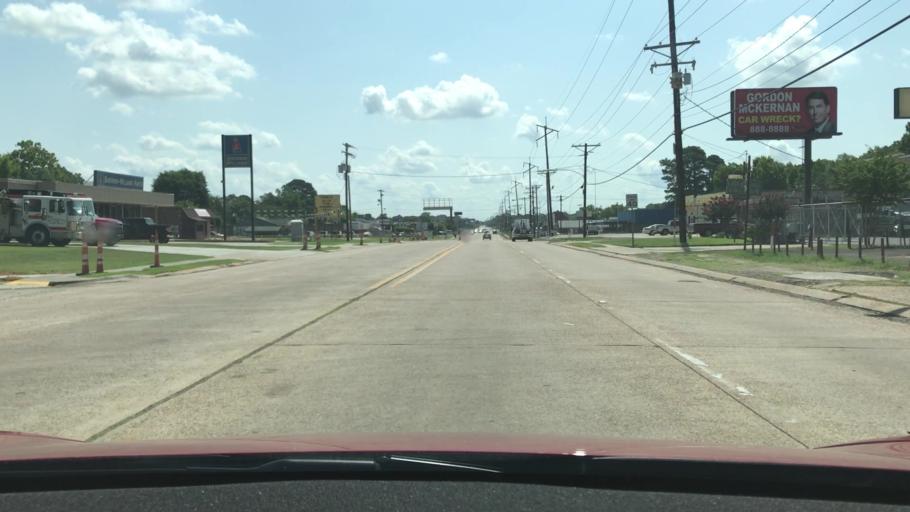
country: US
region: Louisiana
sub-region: Caddo Parish
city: Shreveport
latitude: 32.4420
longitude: -93.7896
